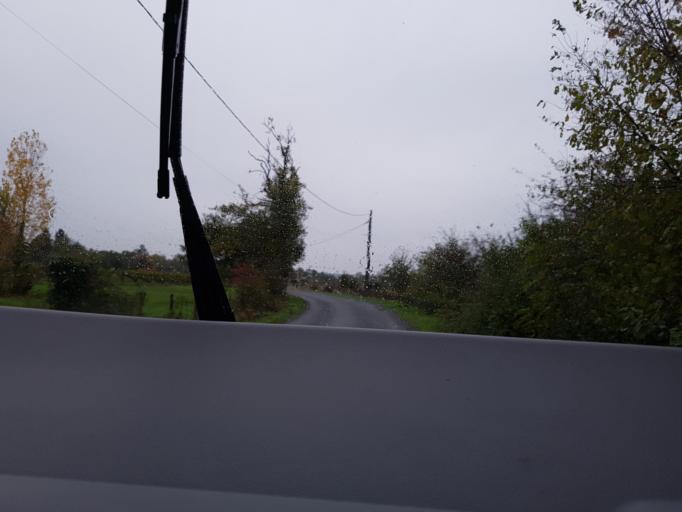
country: FR
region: Aquitaine
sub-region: Departement de la Gironde
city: Cezac
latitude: 45.0852
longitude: -0.4302
